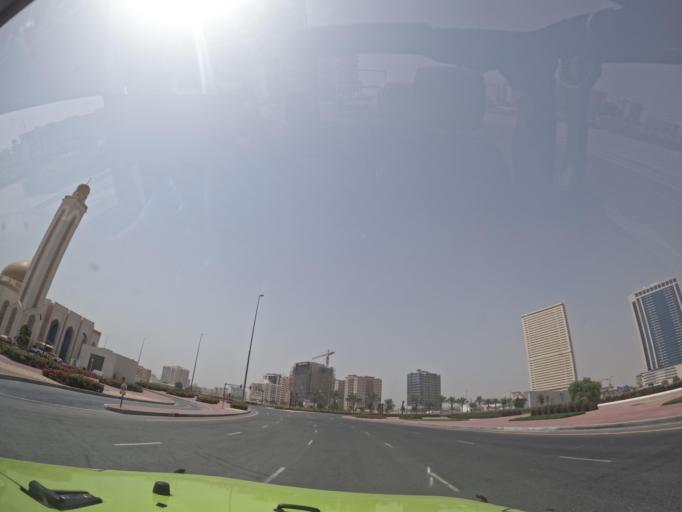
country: AE
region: Dubai
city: Dubai
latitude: 25.0911
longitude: 55.3802
